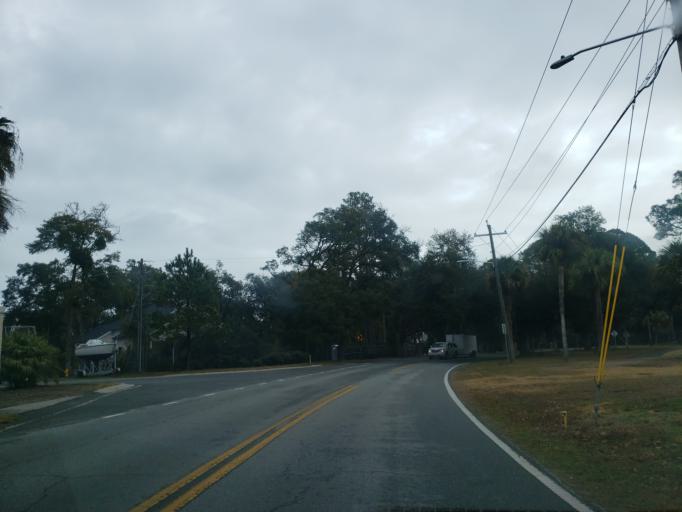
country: US
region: Georgia
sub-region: Chatham County
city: Wilmington Island
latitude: 32.0055
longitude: -80.9980
